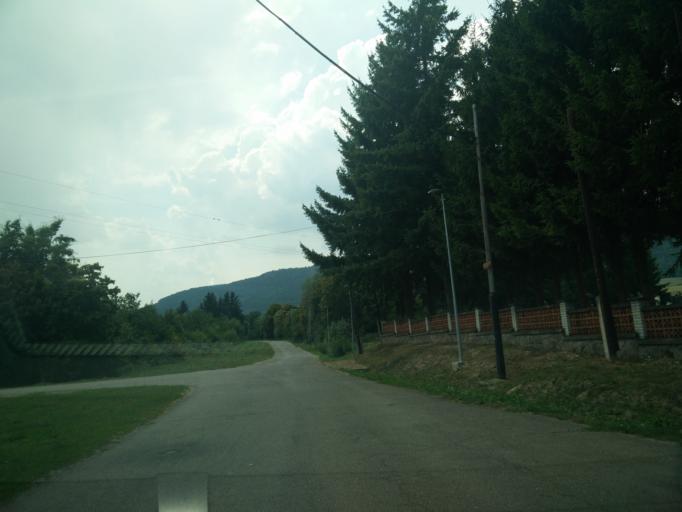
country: SK
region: Banskobystricky
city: Zarnovica
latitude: 48.5650
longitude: 18.7514
